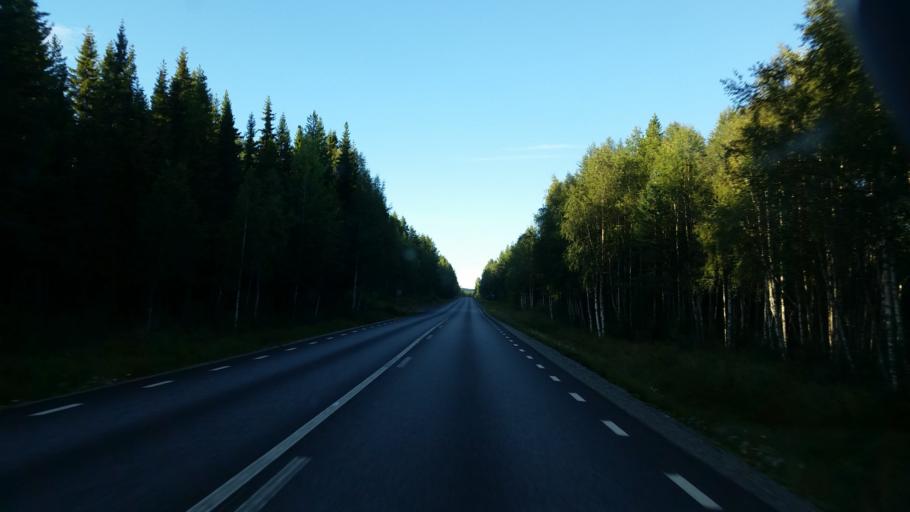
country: SE
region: Vaesterbotten
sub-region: Dorotea Kommun
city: Dorotea
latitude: 64.2394
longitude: 16.3135
